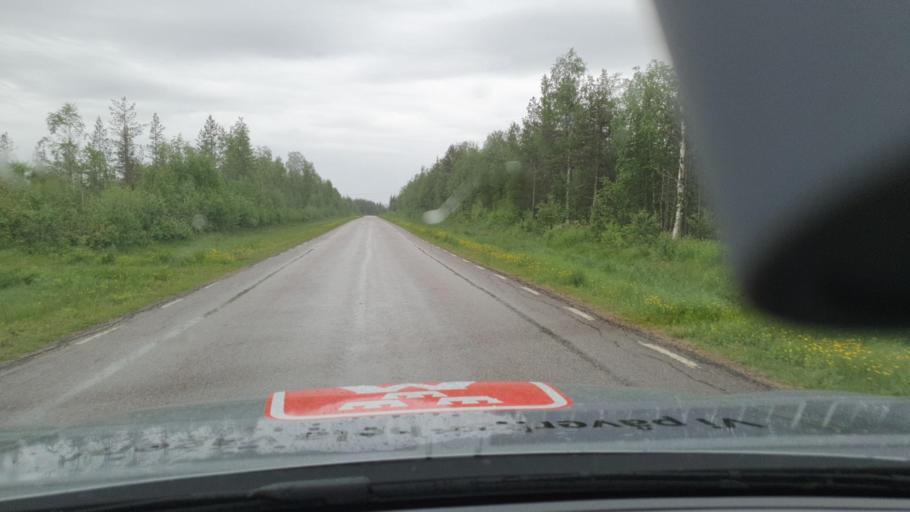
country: SE
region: Norrbotten
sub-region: Pajala Kommun
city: Pajala
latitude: 66.8169
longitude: 23.1172
